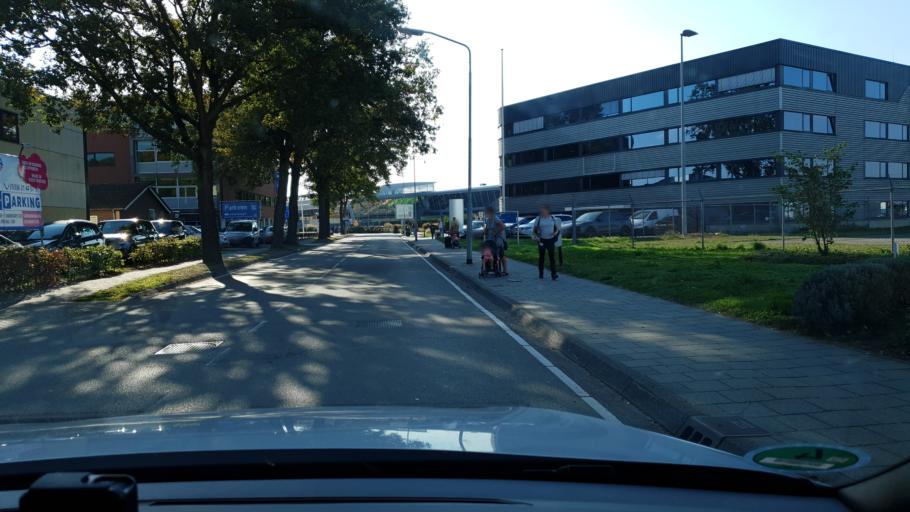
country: NL
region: North Brabant
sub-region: Gemeente Eindhoven
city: Meerhoven
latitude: 51.4596
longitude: 5.3951
